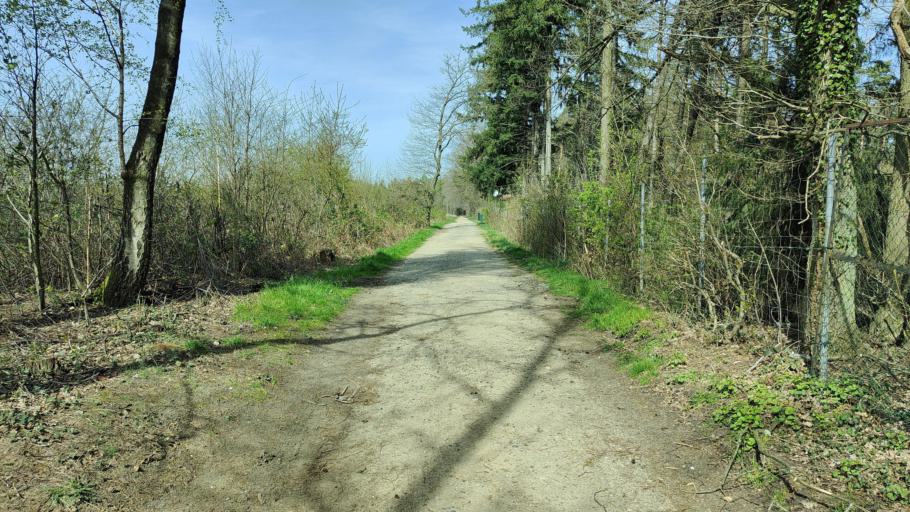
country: DE
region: North Rhine-Westphalia
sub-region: Regierungsbezirk Koln
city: Wassenberg
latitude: 51.1345
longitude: 6.1473
